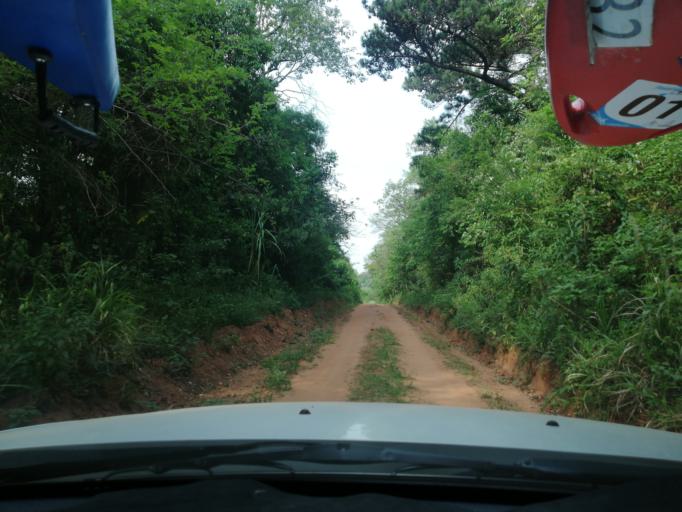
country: AR
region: Misiones
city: Santa Ana
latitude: -27.3037
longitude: -55.5792
